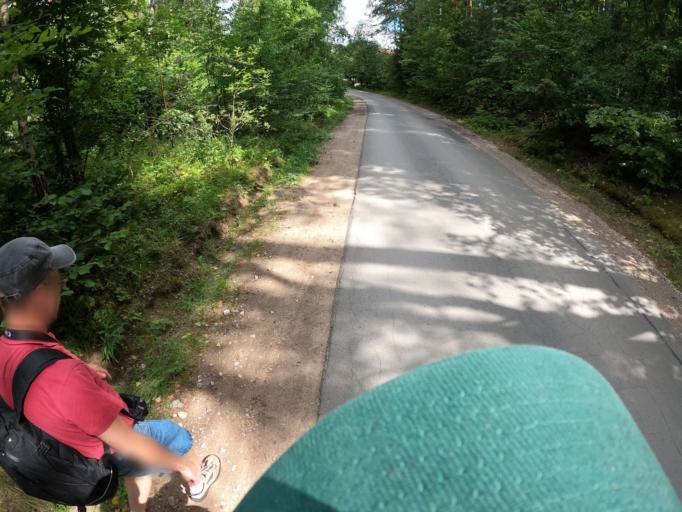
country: LT
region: Alytaus apskritis
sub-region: Alytus
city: Alytus
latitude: 54.4324
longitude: 24.0867
